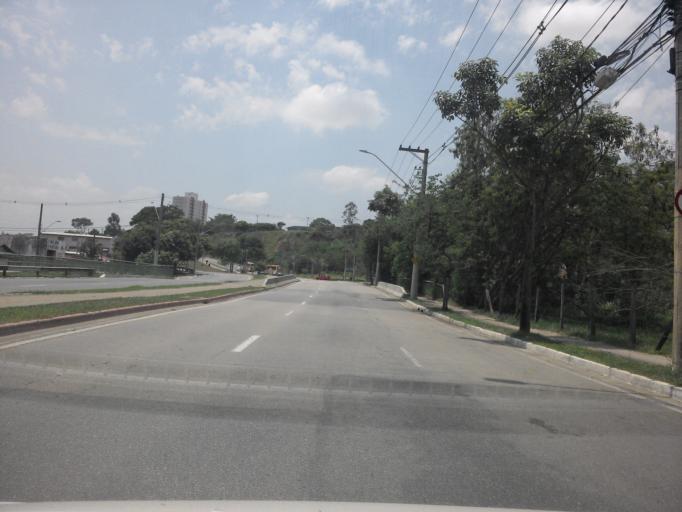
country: BR
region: Sao Paulo
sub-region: Sao Jose Dos Campos
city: Sao Jose dos Campos
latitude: -23.1692
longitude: -45.8097
